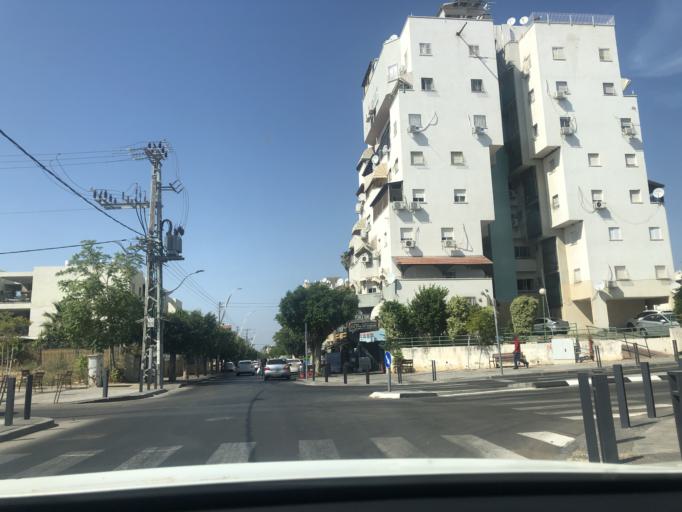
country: IL
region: Central District
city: Lod
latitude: 31.9509
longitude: 34.8943
